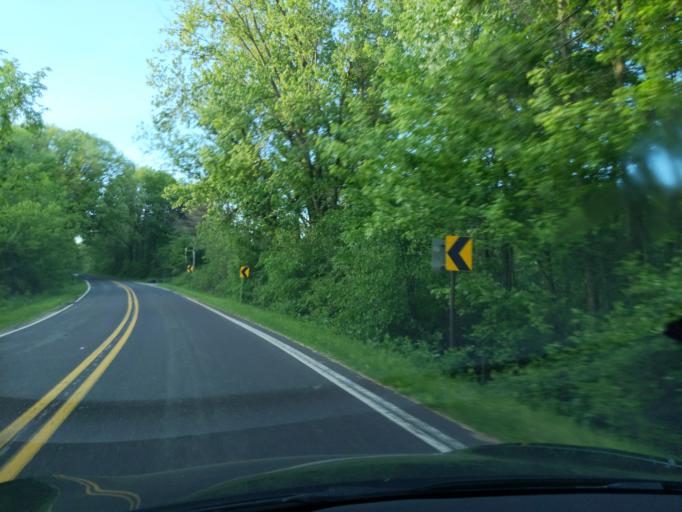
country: US
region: Michigan
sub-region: Ingham County
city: Leslie
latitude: 42.4947
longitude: -84.3158
